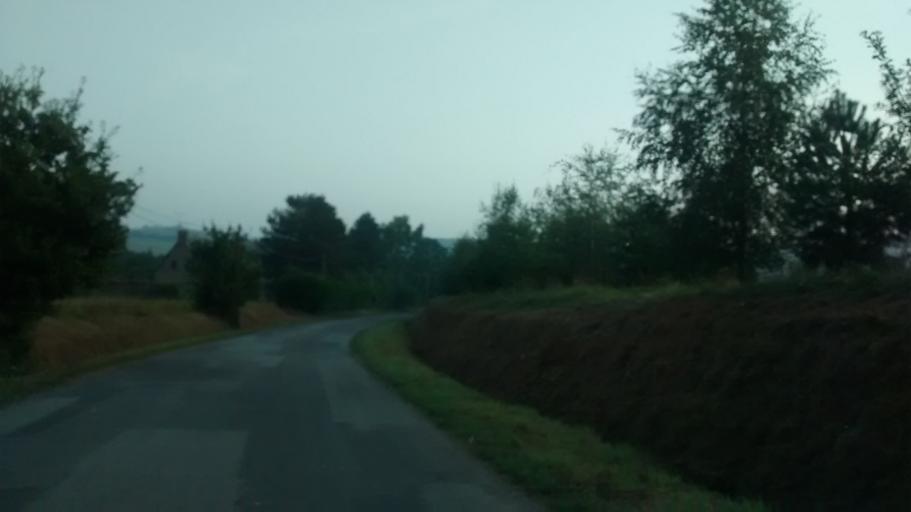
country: FR
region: Brittany
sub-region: Departement d'Ille-et-Vilaine
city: Montreuil-sous-Perouse
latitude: 48.1398
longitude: -1.2533
